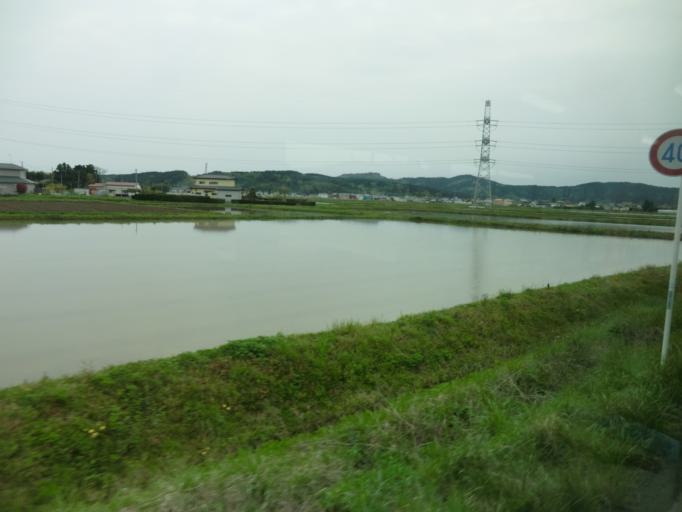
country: JP
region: Miyagi
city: Wakuya
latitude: 38.5189
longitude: 141.2028
